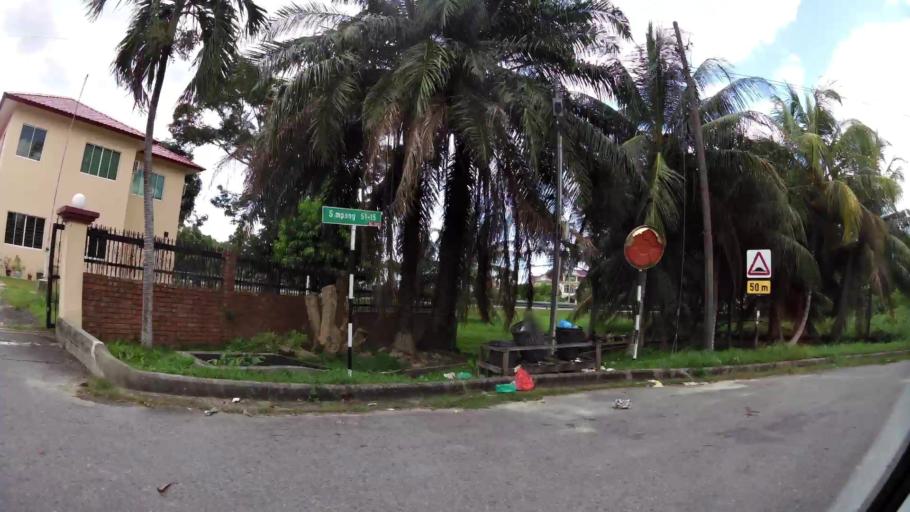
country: BN
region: Brunei and Muara
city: Bandar Seri Begawan
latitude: 4.9527
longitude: 114.9576
